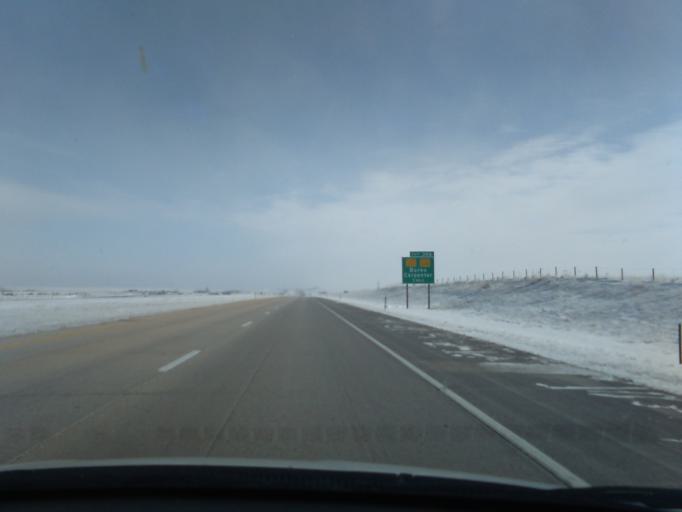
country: US
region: Wyoming
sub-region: Laramie County
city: Pine Bluffs
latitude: 41.1574
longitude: -104.3736
